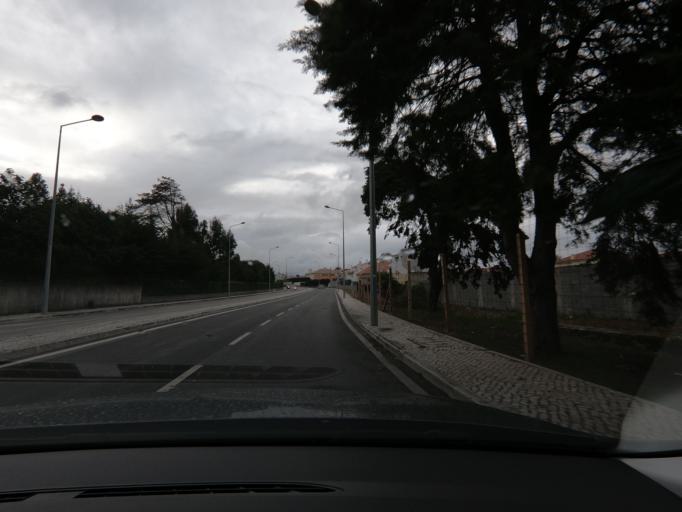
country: PT
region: Lisbon
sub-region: Cascais
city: Sao Domingos de Rana
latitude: 38.7105
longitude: -9.3336
